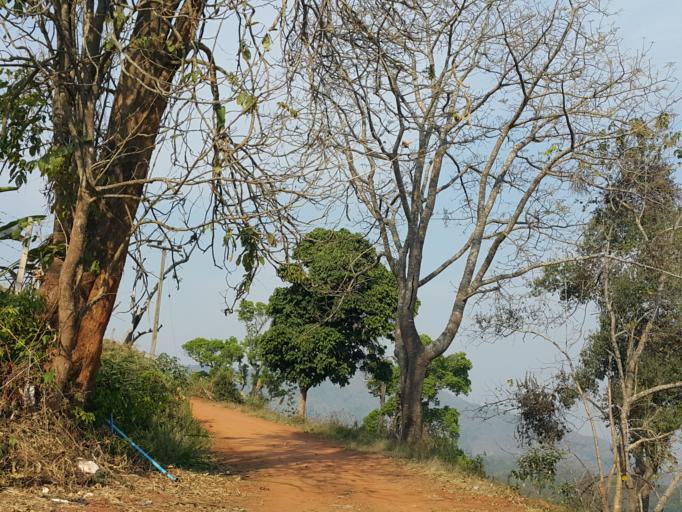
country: TH
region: Chiang Mai
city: Samoeng
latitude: 18.9014
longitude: 98.7947
